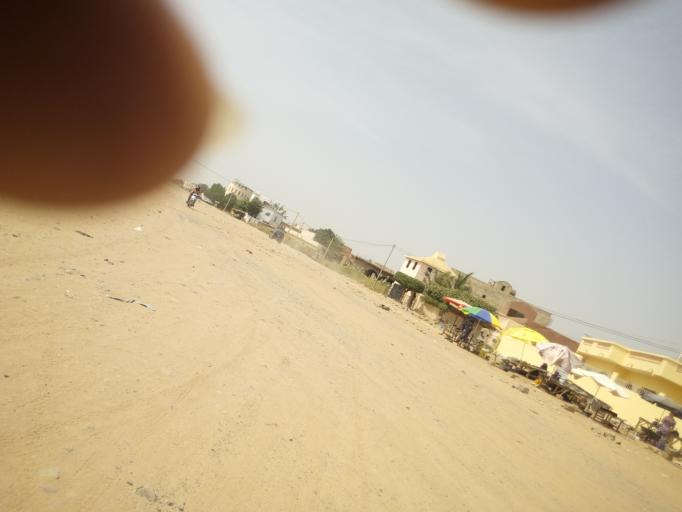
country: ML
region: Kayes
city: Kayes
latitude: 14.4330
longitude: -11.4353
